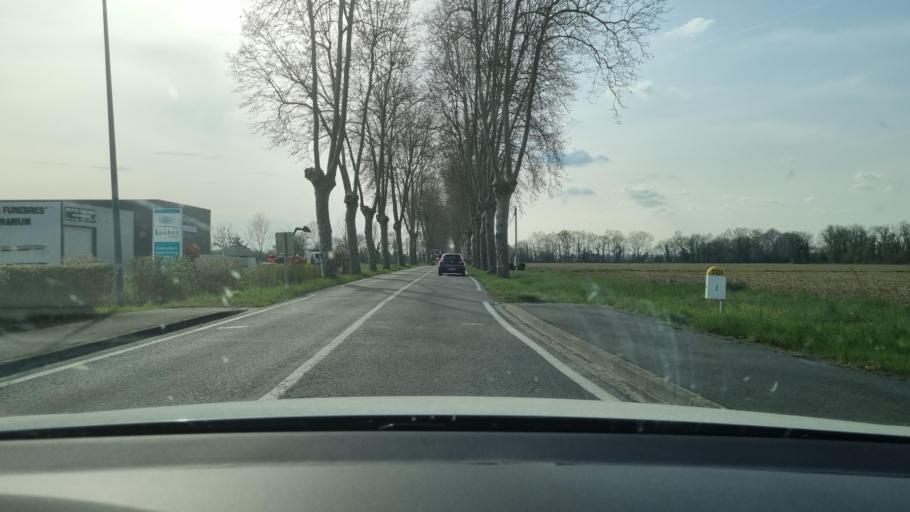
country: FR
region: Midi-Pyrenees
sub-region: Departement des Hautes-Pyrenees
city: Rabastens-de-Bigorre
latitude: 43.3874
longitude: 0.1405
